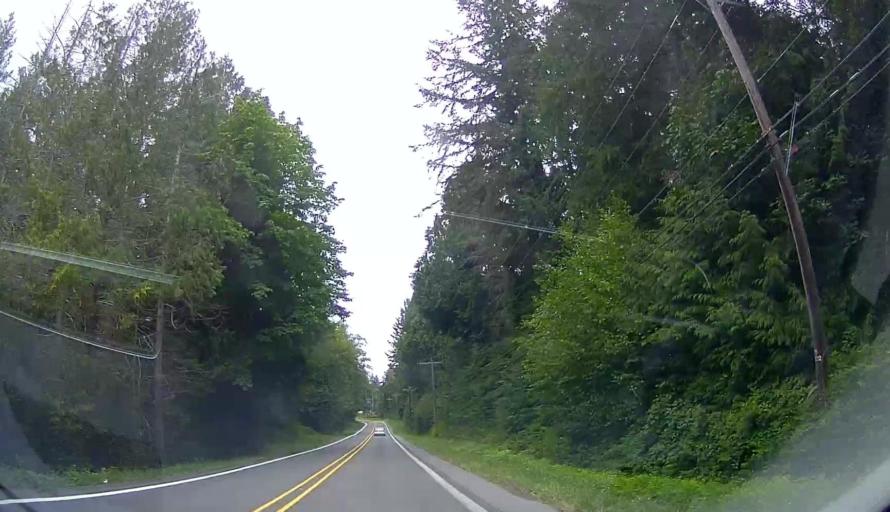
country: US
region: Washington
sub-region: Snohomish County
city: Tulalip
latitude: 48.1059
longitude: -122.3284
